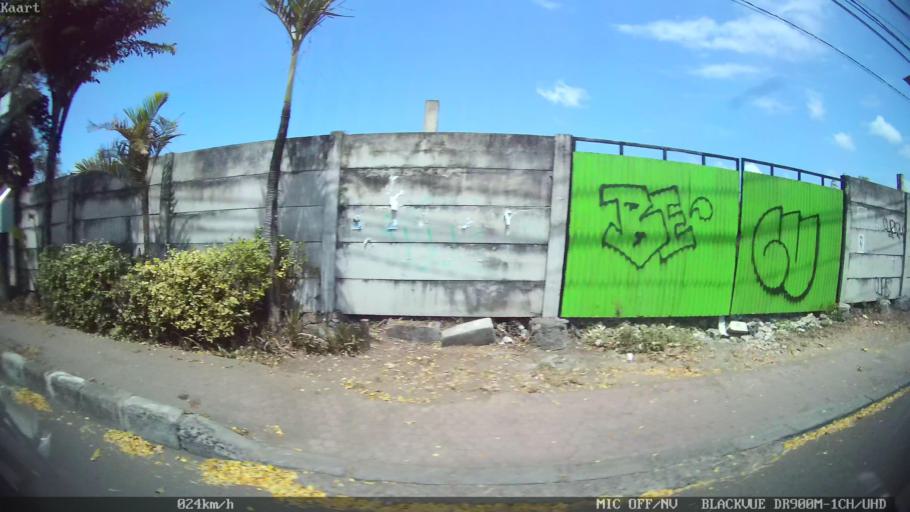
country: ID
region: Bali
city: Denpasar
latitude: -8.6544
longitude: 115.2073
